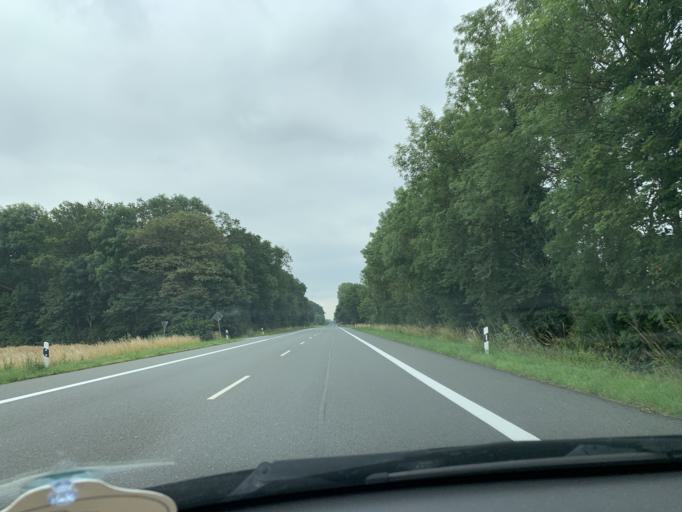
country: DE
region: North Rhine-Westphalia
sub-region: Regierungsbezirk Munster
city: Warendorf
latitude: 51.9191
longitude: 8.0380
